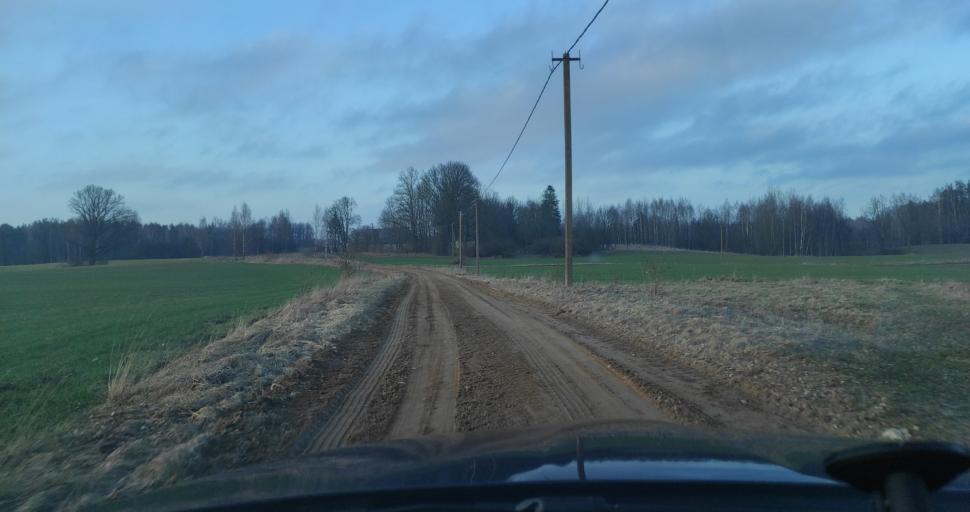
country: LV
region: Aizpute
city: Aizpute
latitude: 56.8002
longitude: 21.8040
